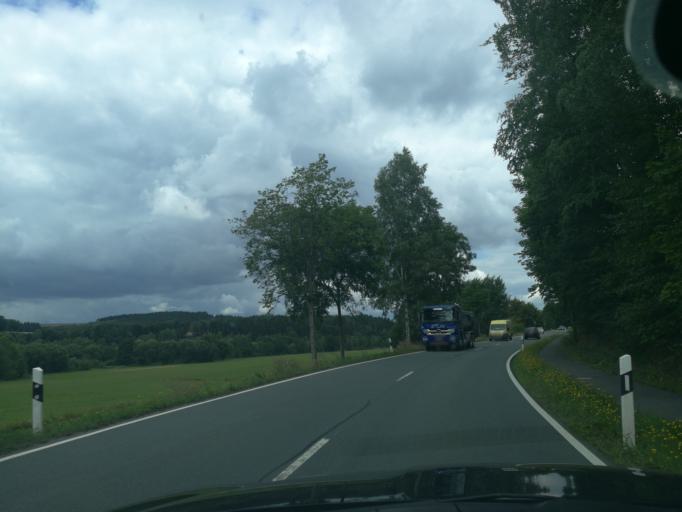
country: DE
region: Saxony
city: Adorf
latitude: 50.3532
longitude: 12.2282
